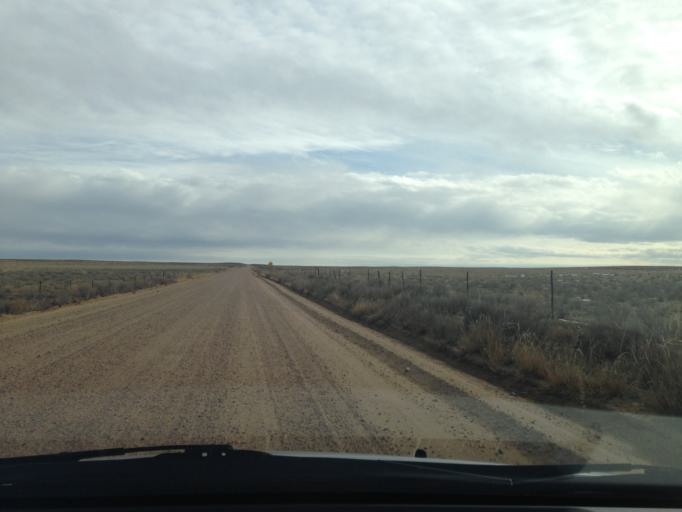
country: US
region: Colorado
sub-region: Weld County
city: Keenesburg
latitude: 40.2653
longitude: -104.2068
